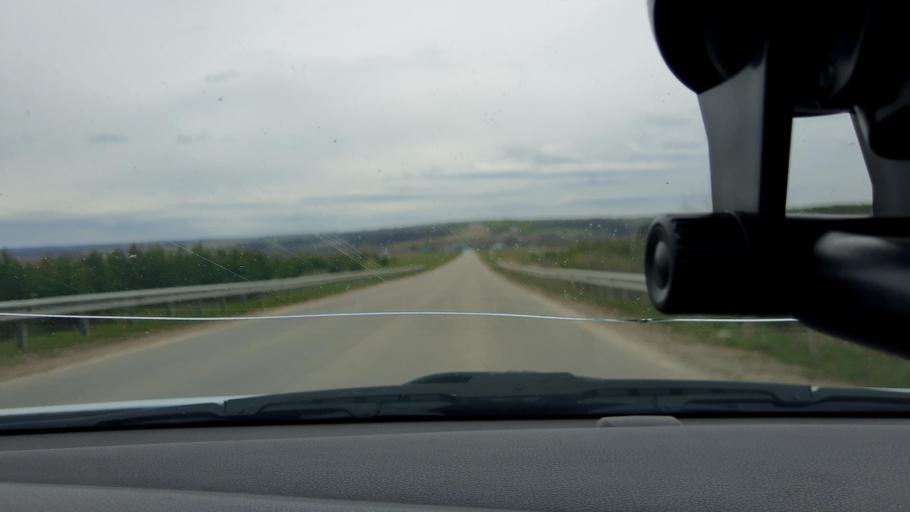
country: RU
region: Bashkortostan
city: Blagoveshchensk
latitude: 55.1181
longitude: 56.0659
